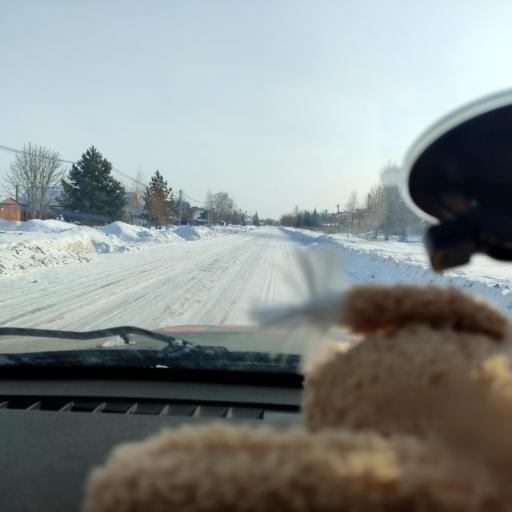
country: RU
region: Samara
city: Podstepki
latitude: 53.5107
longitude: 49.1205
